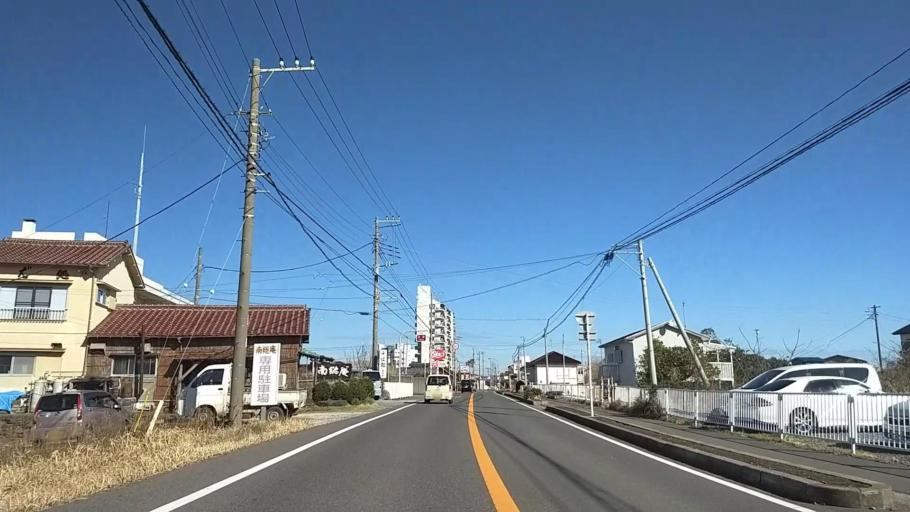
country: JP
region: Chiba
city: Tateyama
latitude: 34.9753
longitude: 139.9631
